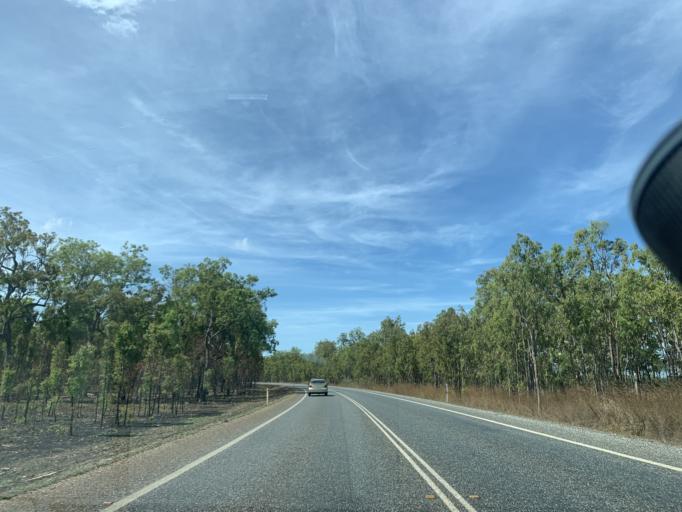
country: AU
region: Queensland
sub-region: Tablelands
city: Mareeba
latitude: -17.0810
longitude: 145.4361
